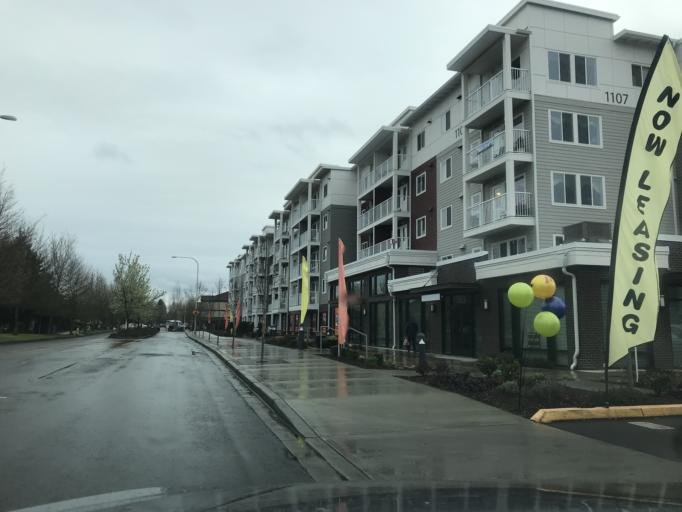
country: US
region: Washington
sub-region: King County
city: Auburn
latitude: 47.3178
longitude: -122.2288
